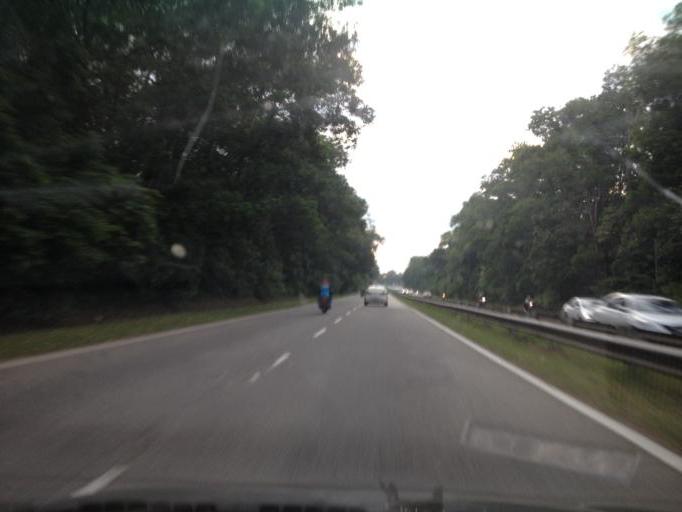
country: MY
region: Kedah
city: Sungai Petani
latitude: 5.6081
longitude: 100.5094
